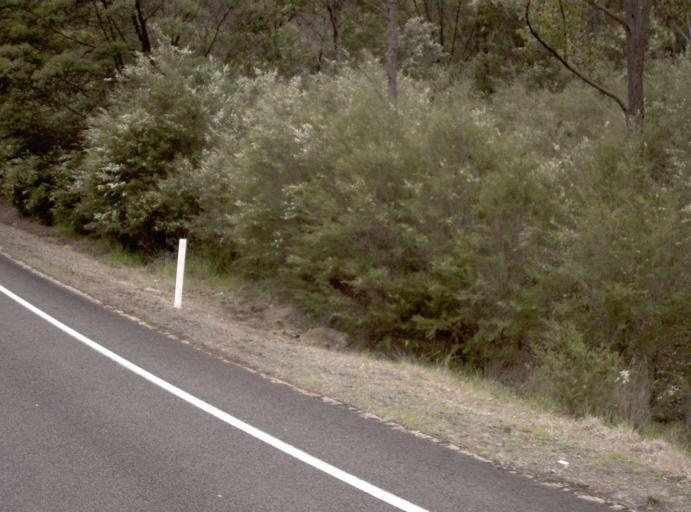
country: AU
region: New South Wales
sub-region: Bombala
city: Bombala
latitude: -37.2474
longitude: 149.2548
